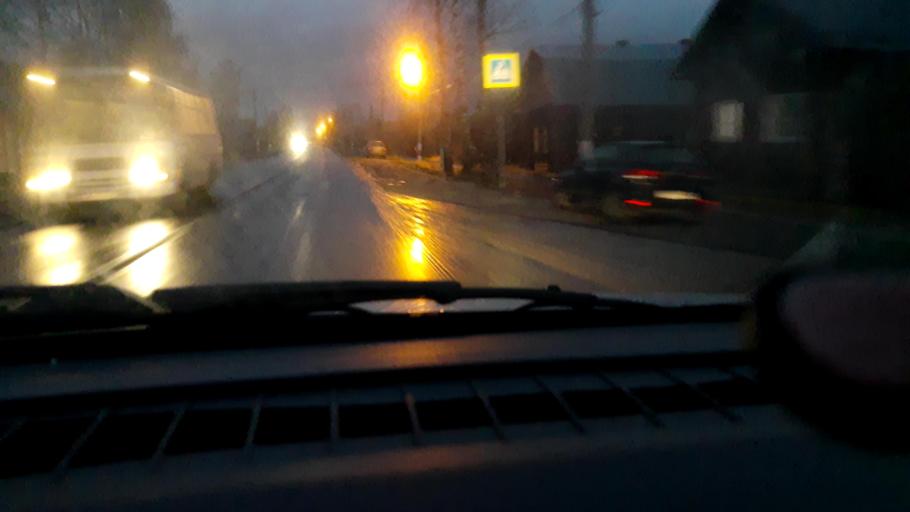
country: RU
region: Nizjnij Novgorod
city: Uren'
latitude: 57.4534
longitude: 45.7805
